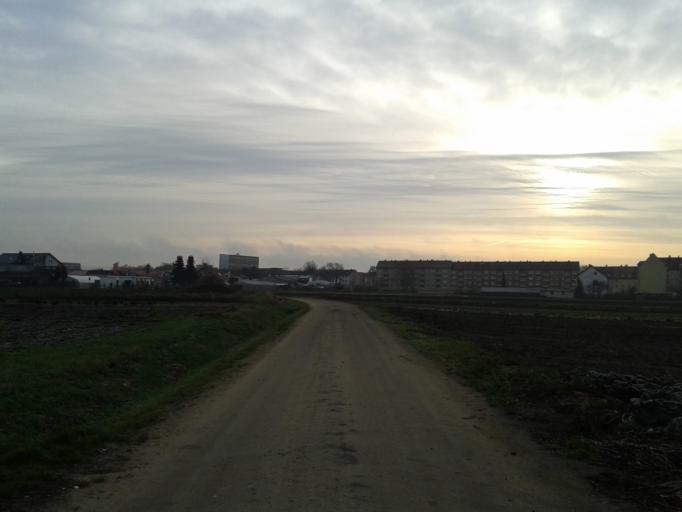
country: DE
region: Bavaria
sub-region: Upper Franconia
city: Bamberg
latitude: 49.9099
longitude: 10.8963
